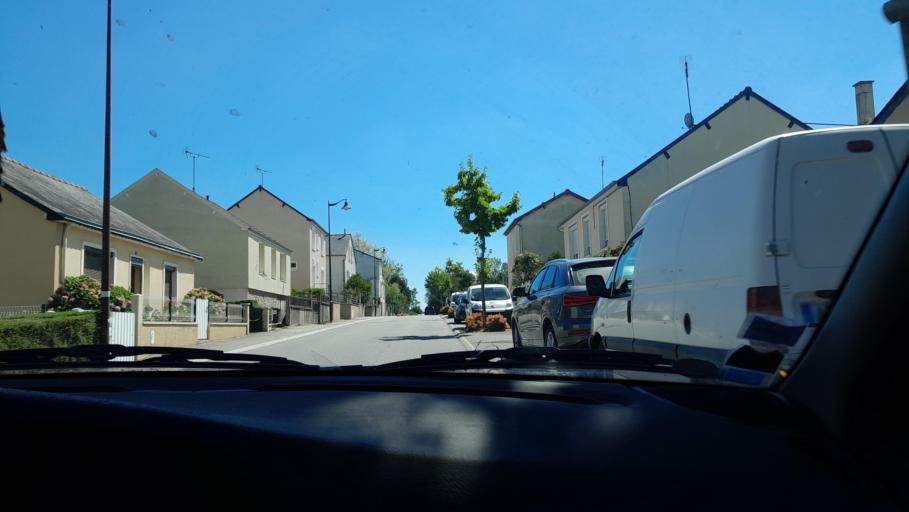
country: FR
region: Pays de la Loire
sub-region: Departement de Maine-et-Loire
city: Pouance
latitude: 47.7368
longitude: -1.1776
